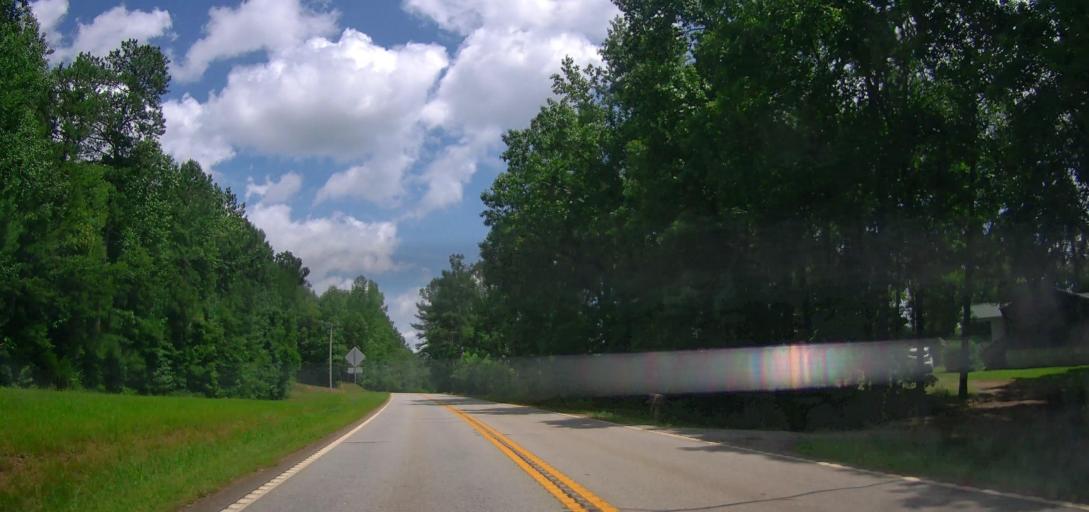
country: US
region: Georgia
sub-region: Heard County
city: Franklin
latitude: 33.3118
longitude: -85.1441
